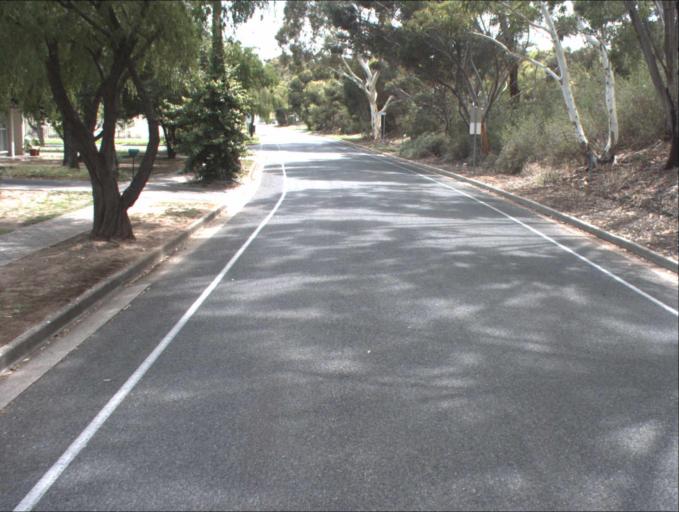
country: AU
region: South Australia
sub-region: Campbelltown
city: Paradise
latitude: -34.8655
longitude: 138.6651
